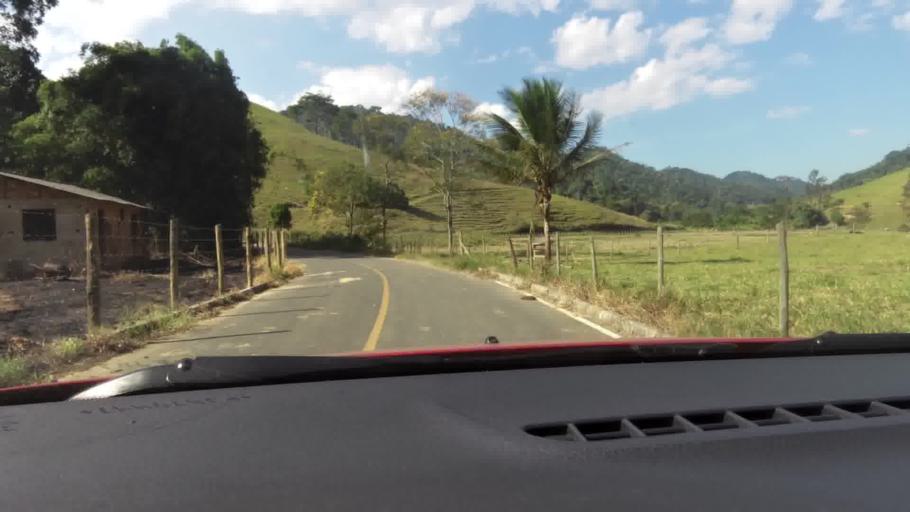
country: BR
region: Espirito Santo
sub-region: Guarapari
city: Guarapari
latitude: -20.5793
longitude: -40.5607
